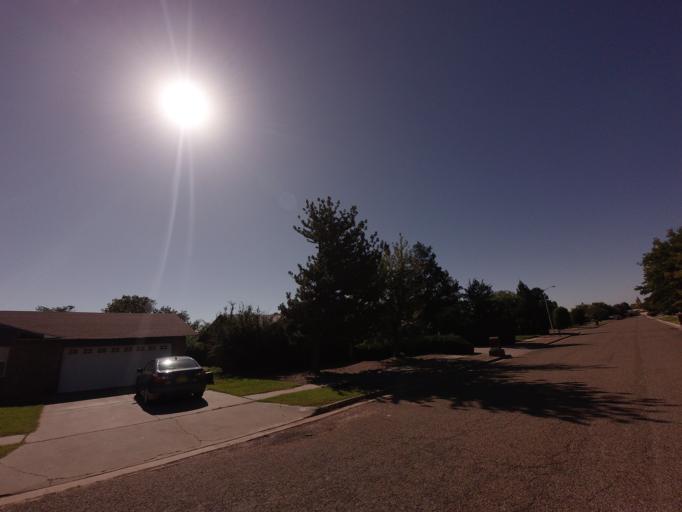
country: US
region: New Mexico
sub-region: Curry County
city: Clovis
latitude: 34.4250
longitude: -103.1842
